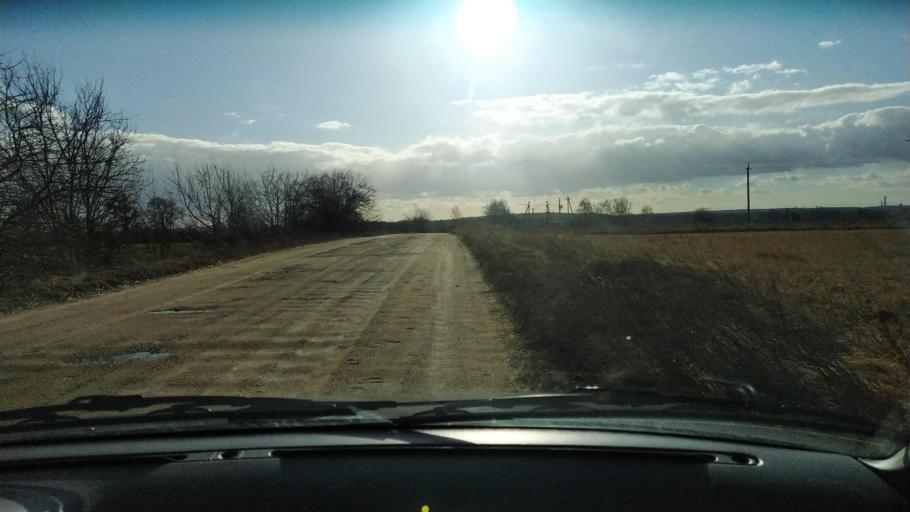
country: BY
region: Brest
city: Kamyanyets
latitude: 52.4252
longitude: 23.8206
